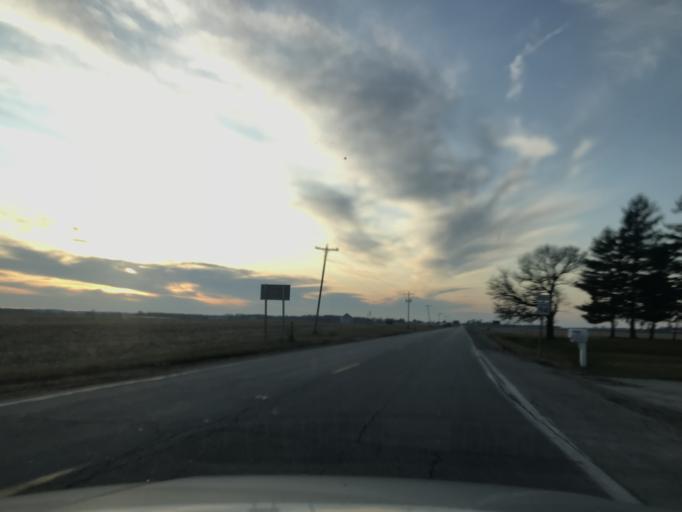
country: US
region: Illinois
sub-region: Warren County
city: Monmouth
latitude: 41.0247
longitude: -90.7466
